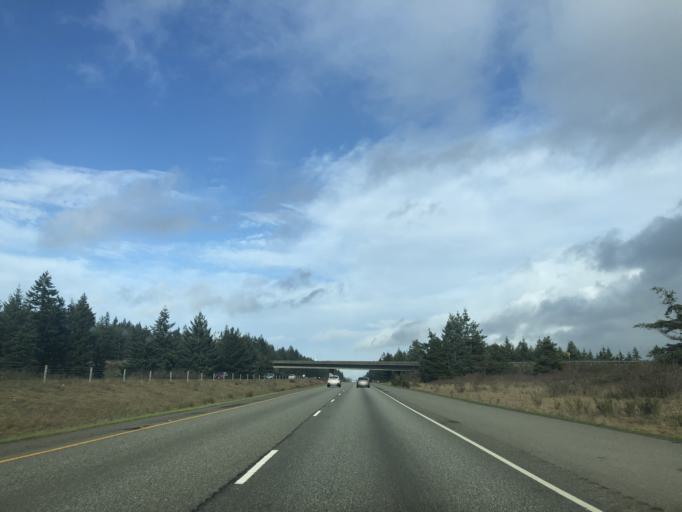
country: US
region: Washington
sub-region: Kitsap County
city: Bangor Trident Base
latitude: 47.6986
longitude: -122.6854
